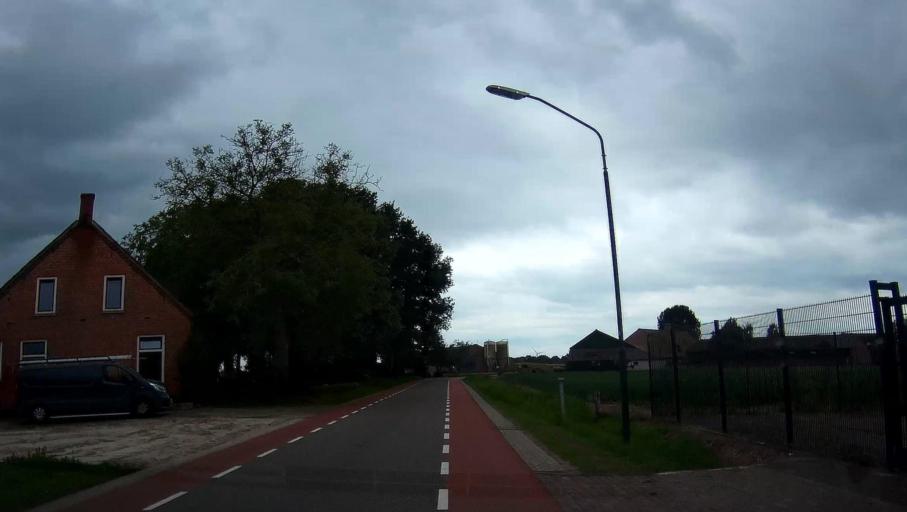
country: NL
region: North Brabant
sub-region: Gemeente Bladel en Netersel
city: Bladel
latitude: 51.3522
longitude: 5.1712
